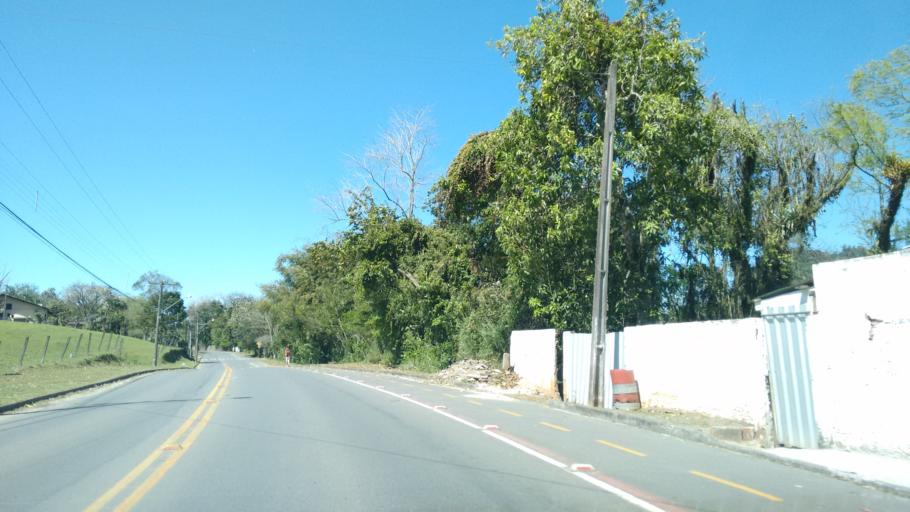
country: BR
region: Santa Catarina
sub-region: Blumenau
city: Blumenau
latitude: -26.8887
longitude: -49.1334
